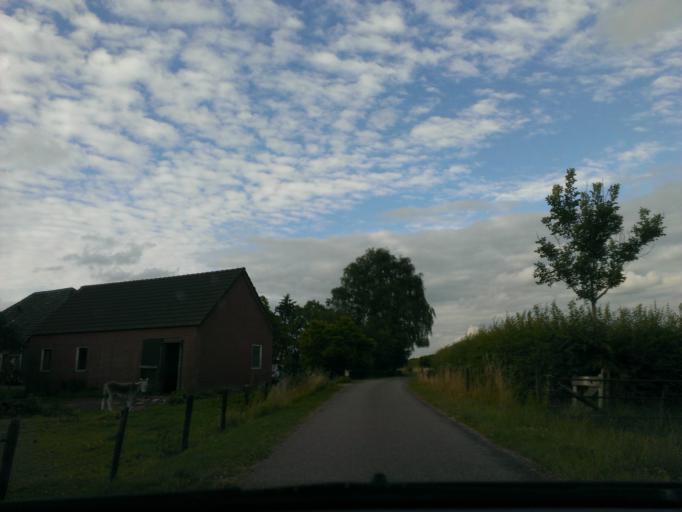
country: NL
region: Gelderland
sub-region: Gemeente Voorst
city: Twello
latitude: 52.2645
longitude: 6.1156
